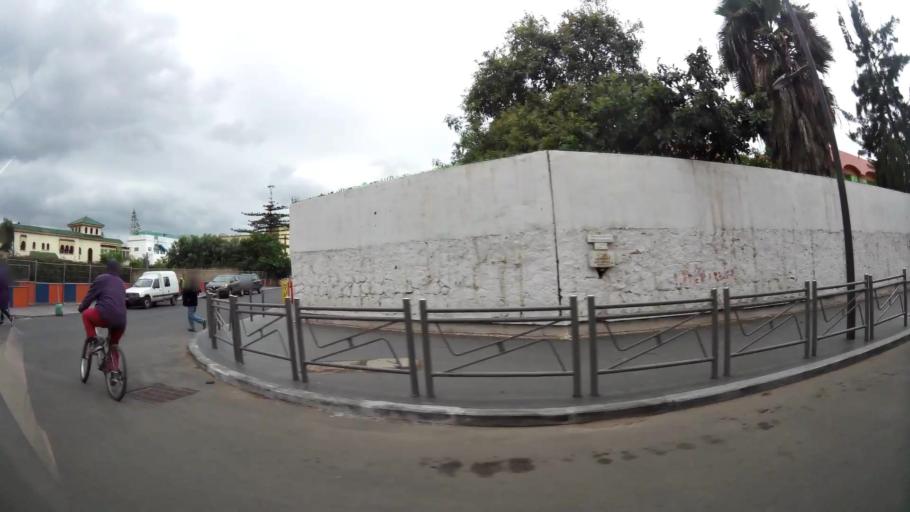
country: MA
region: Grand Casablanca
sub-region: Casablanca
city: Casablanca
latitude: 33.5695
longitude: -7.6222
